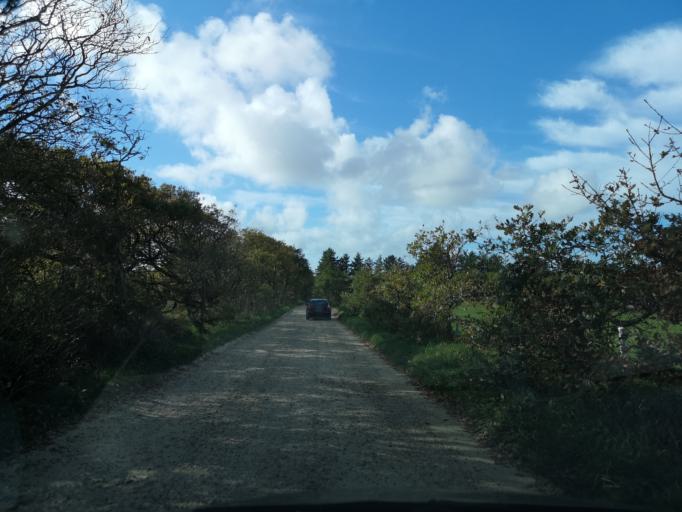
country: DK
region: South Denmark
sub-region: Varde Kommune
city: Oksbol
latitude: 55.7389
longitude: 8.2359
